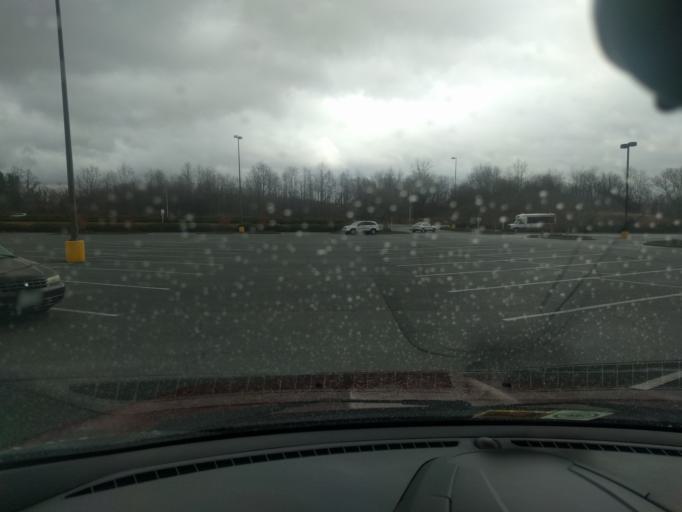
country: US
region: Virginia
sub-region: Pulaski County
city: Pulaski
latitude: 37.0619
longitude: -80.7613
